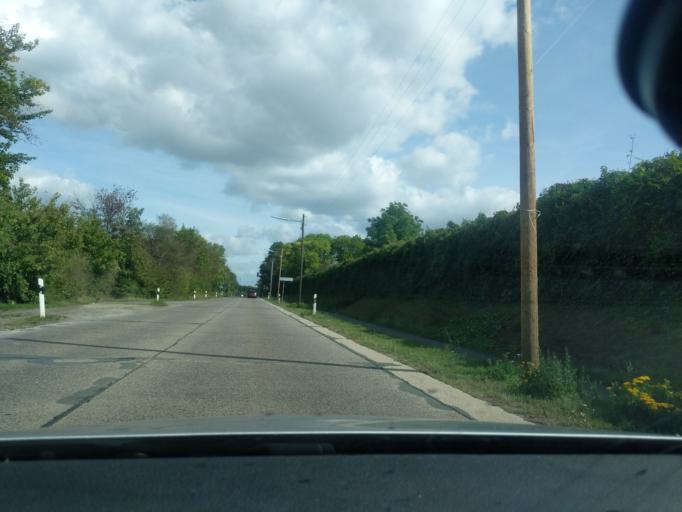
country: DE
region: Lower Saxony
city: Osnabrueck
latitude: 52.2989
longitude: 8.0455
